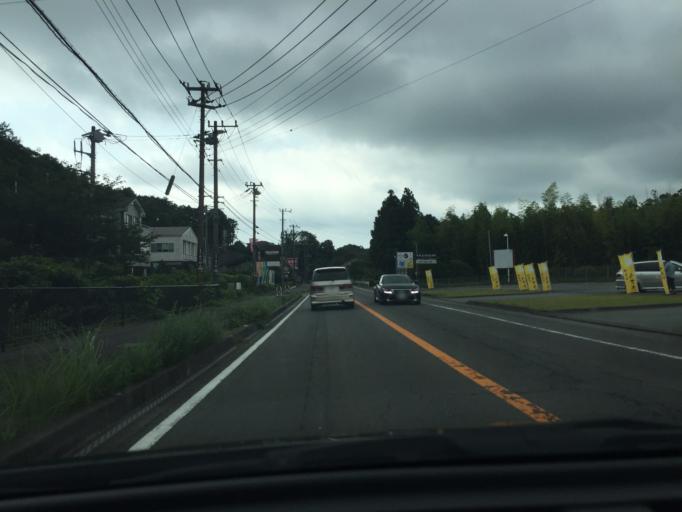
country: JP
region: Shizuoka
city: Ito
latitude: 34.9201
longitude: 139.1197
